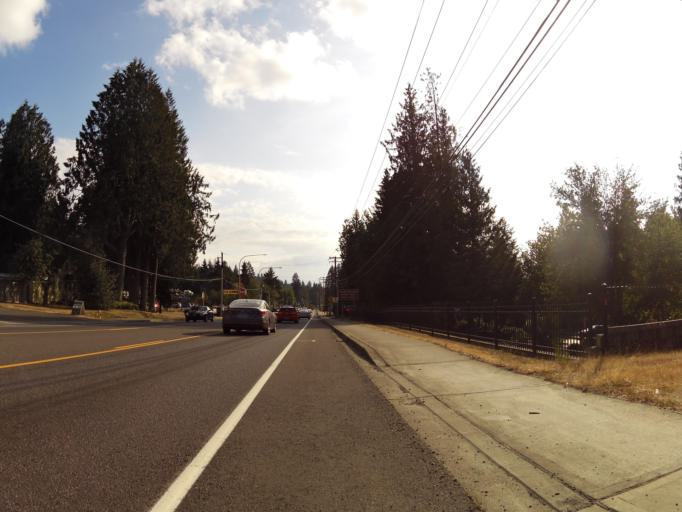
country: US
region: Washington
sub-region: Mason County
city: Belfair
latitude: 47.4425
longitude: -122.8329
